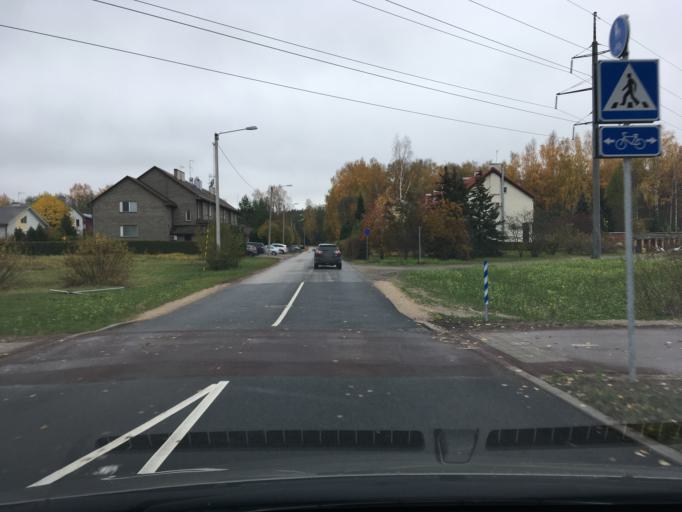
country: EE
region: Tartu
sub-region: Tartu linn
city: Tartu
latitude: 58.3590
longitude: 26.7781
